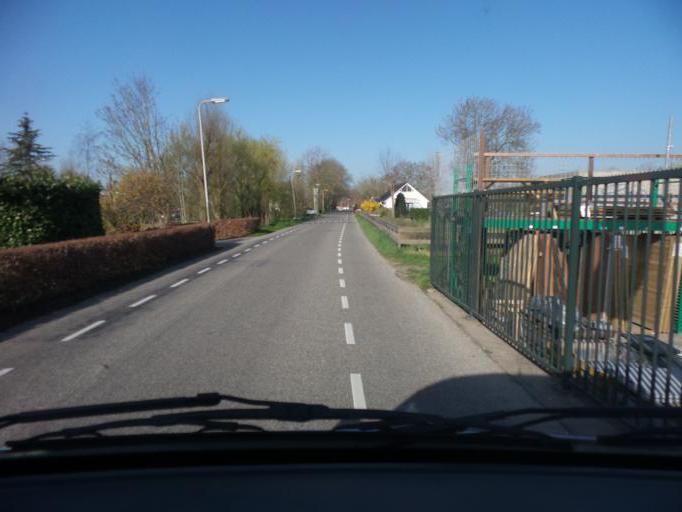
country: NL
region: South Holland
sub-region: Bodegraven-Reeuwijk
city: Bodegraven
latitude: 52.0801
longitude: 4.7670
